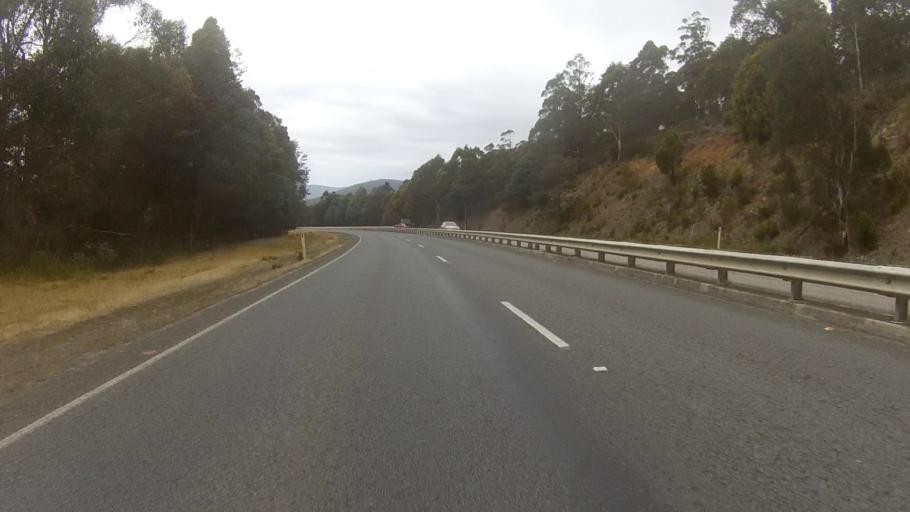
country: AU
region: Tasmania
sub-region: Kingborough
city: Margate
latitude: -42.9849
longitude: 147.1802
